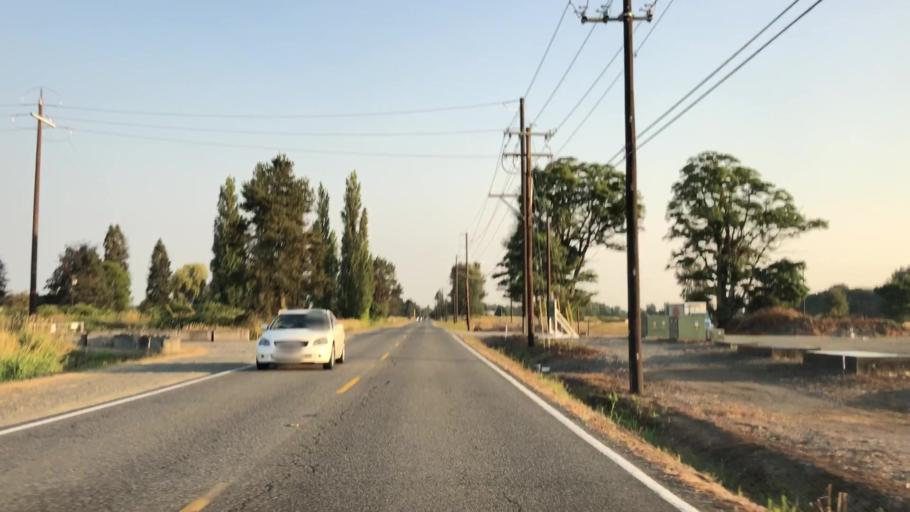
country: US
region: Washington
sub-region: Snohomish County
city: Smokey Point
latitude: 48.1437
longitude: -122.1617
